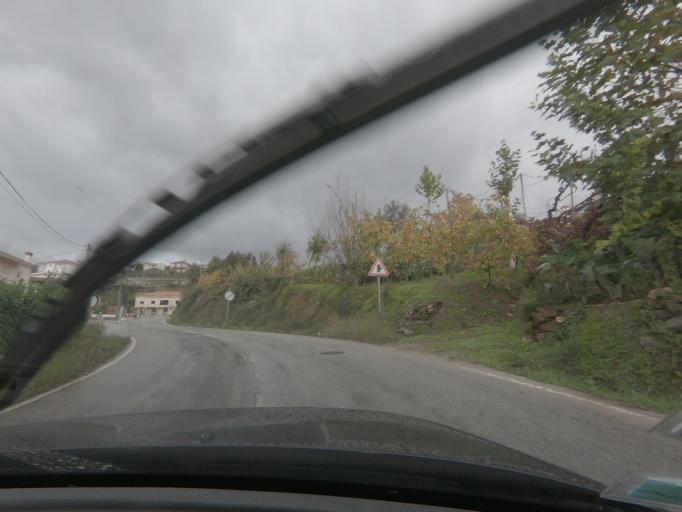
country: PT
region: Vila Real
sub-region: Mondim de Basto
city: Mondim de Basto
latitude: 41.4114
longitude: -7.9726
